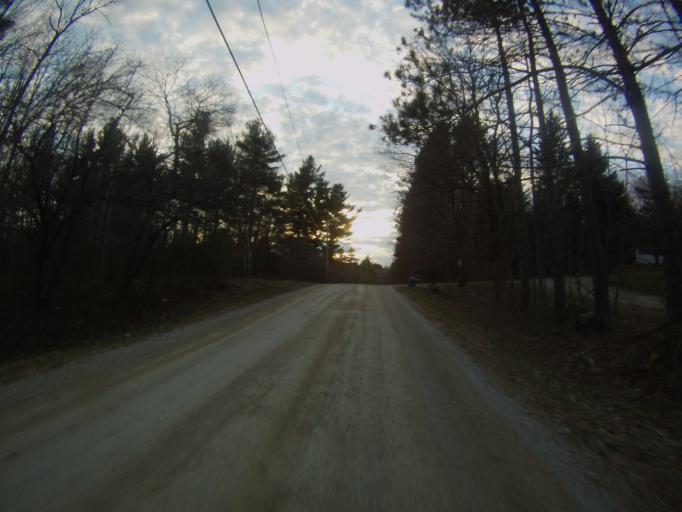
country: US
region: Vermont
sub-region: Rutland County
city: Brandon
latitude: 43.8716
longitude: -73.0128
